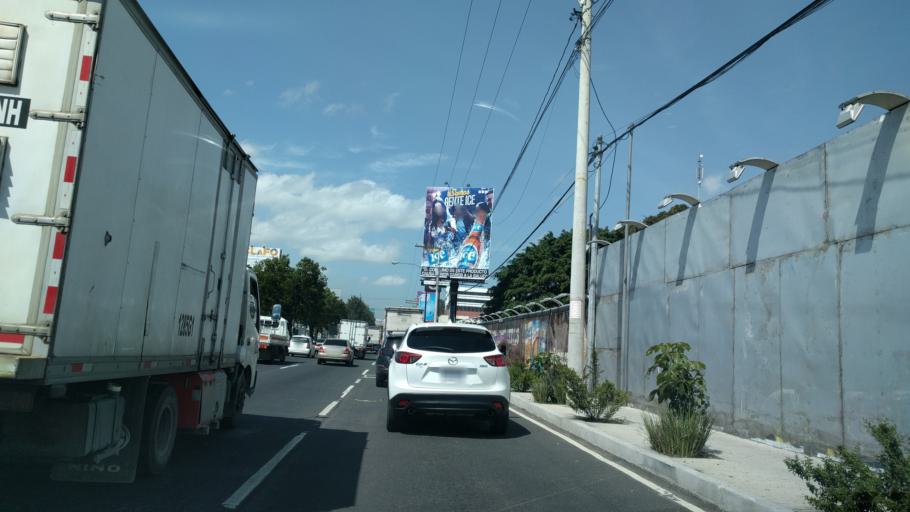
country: GT
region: Guatemala
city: Mixco
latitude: 14.5926
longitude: -90.5592
